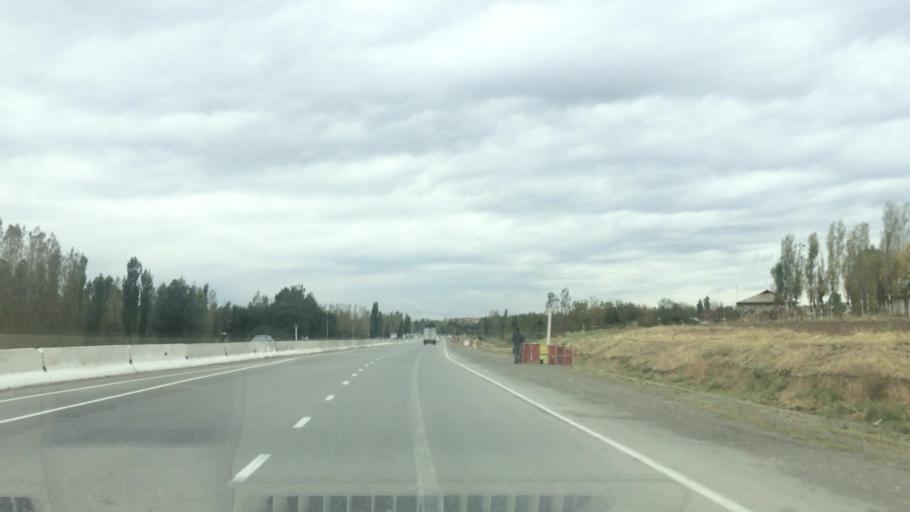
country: UZ
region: Jizzax
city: Jizzax
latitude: 39.9605
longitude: 67.5461
